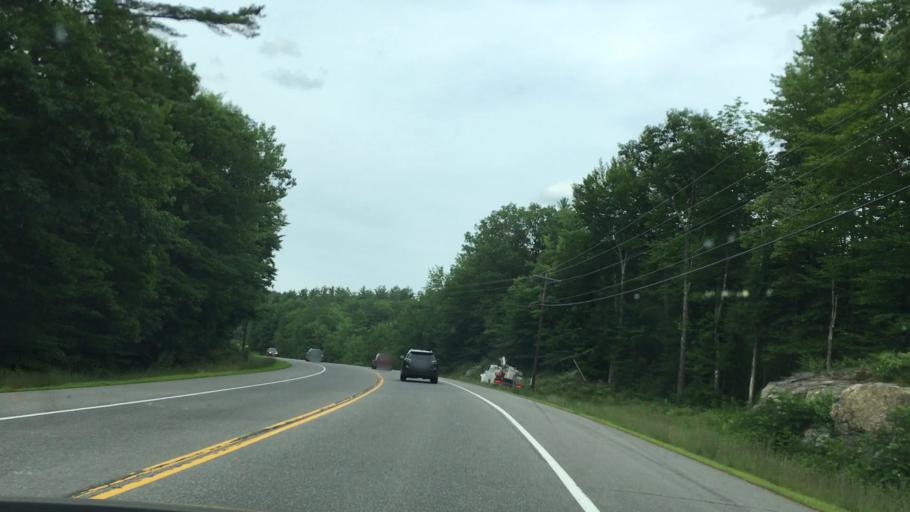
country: US
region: New Hampshire
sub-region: Belknap County
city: Meredith
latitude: 43.6306
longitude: -71.5315
